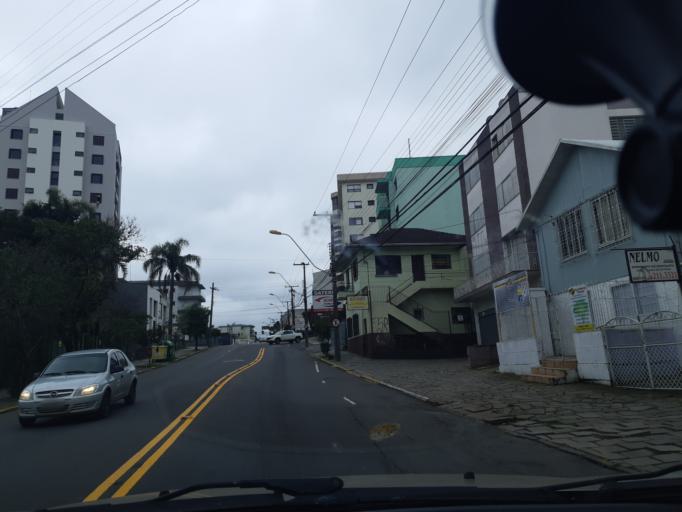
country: BR
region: Rio Grande do Sul
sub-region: Caxias Do Sul
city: Caxias do Sul
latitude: -29.1594
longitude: -51.1952
